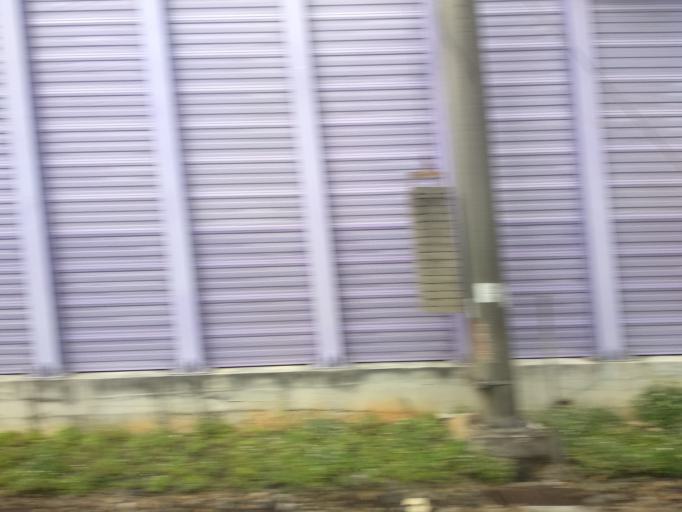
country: TW
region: Taiwan
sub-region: Hsinchu
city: Zhubei
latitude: 24.9056
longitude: 121.0453
